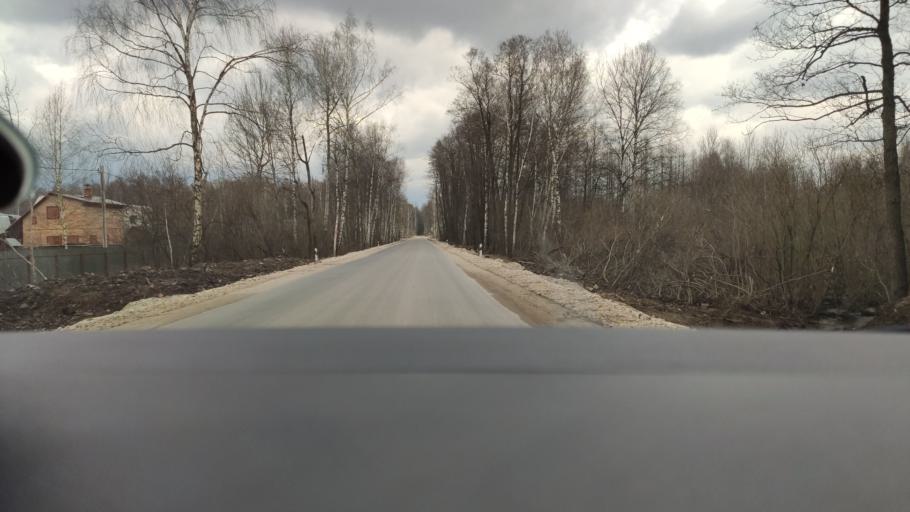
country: RU
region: Moskovskaya
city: Elektrostal'
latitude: 55.7956
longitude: 38.3707
